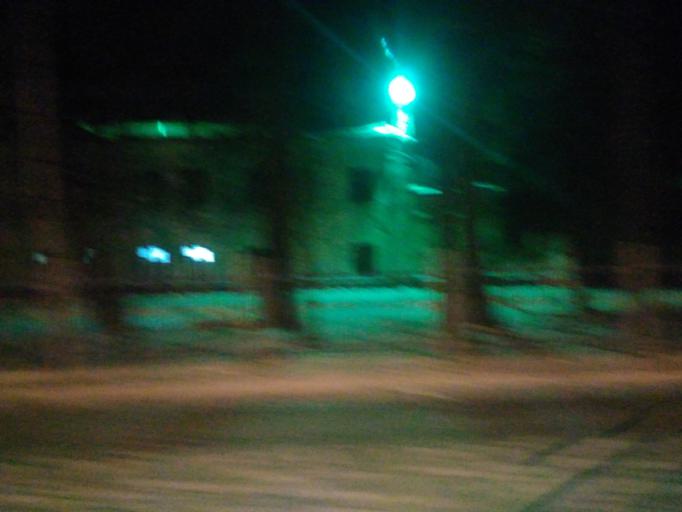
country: RU
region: Ulyanovsk
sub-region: Ulyanovskiy Rayon
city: Ulyanovsk
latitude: 54.3432
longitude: 48.3937
